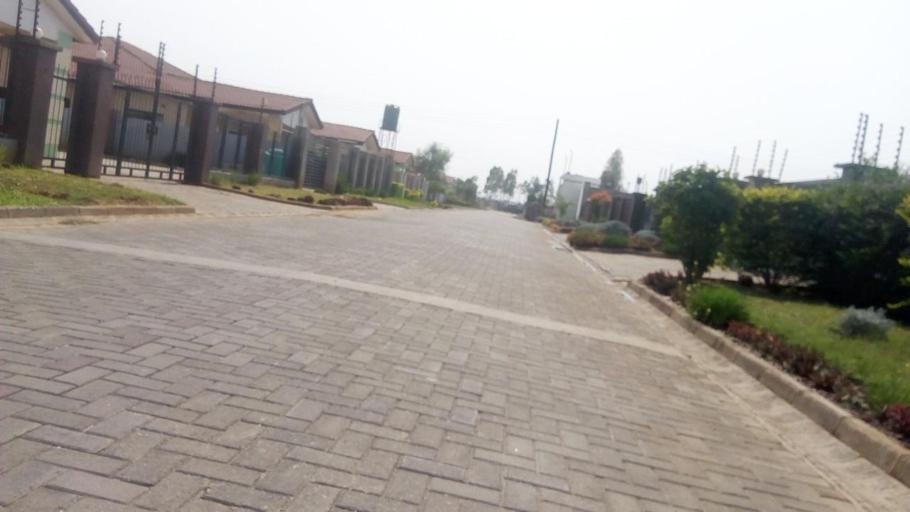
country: ZM
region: Lusaka
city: Lusaka
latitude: -15.3616
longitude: 28.2811
